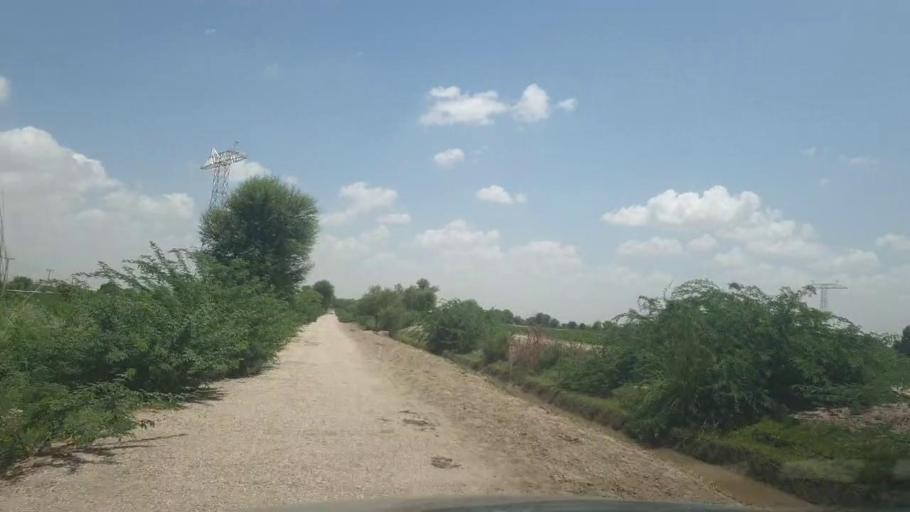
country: PK
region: Sindh
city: Kot Diji
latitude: 27.2586
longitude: 69.0460
